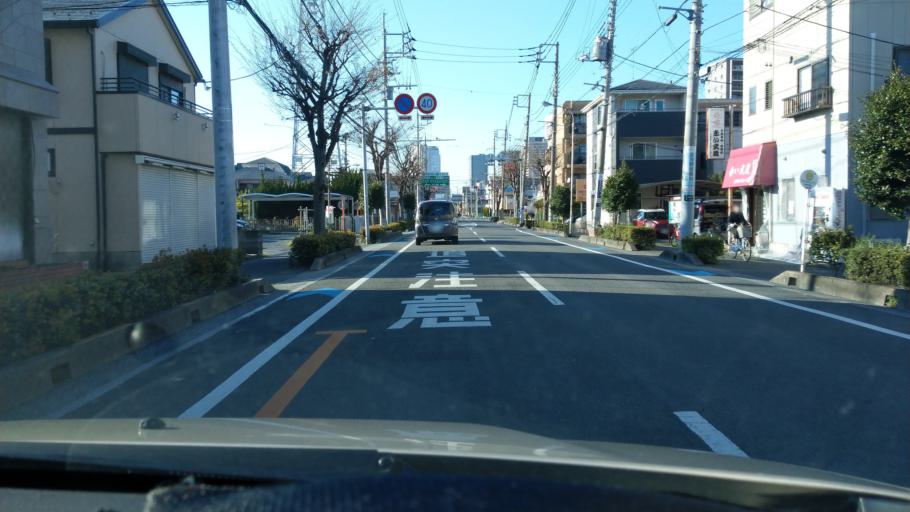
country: JP
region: Saitama
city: Yono
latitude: 35.8957
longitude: 139.6217
